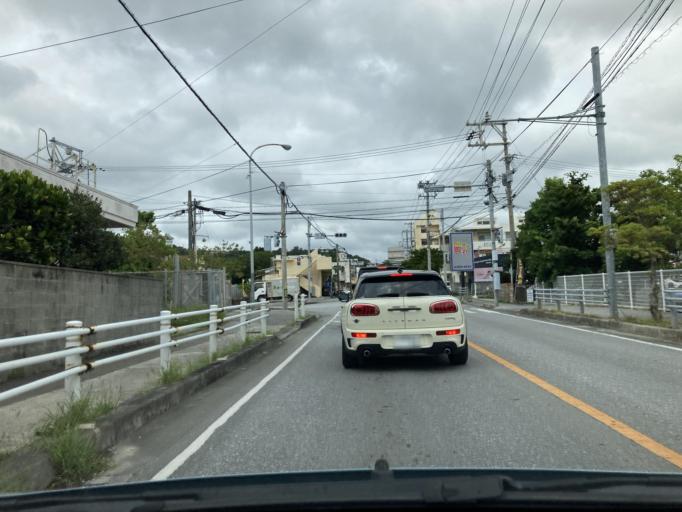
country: JP
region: Okinawa
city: Ginowan
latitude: 26.2290
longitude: 127.7540
